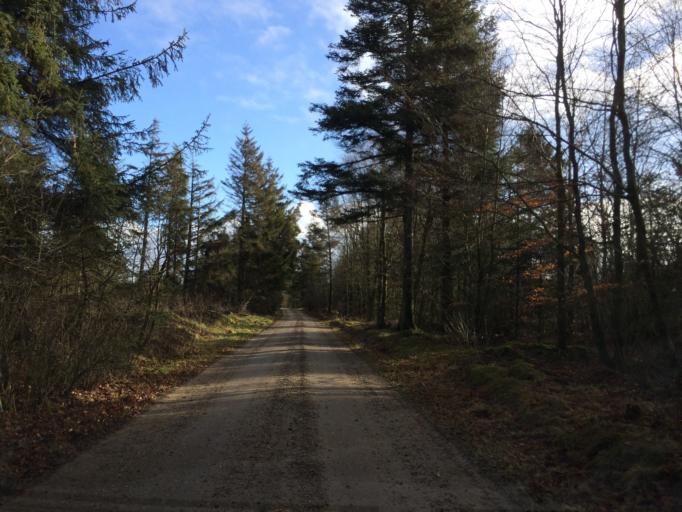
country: DK
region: Central Jutland
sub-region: Holstebro Kommune
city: Ulfborg
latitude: 56.2785
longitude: 8.3565
